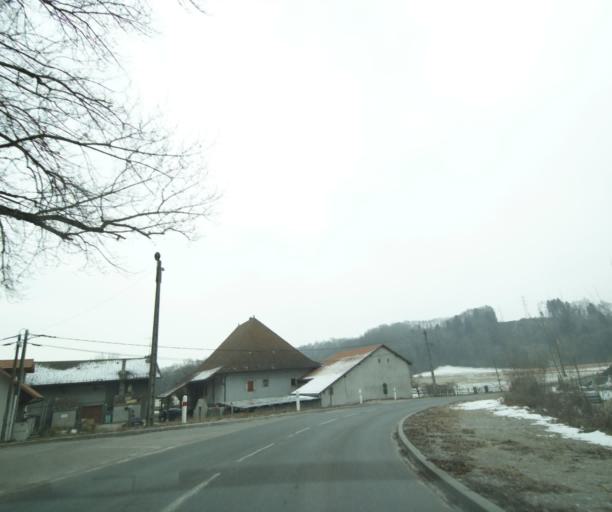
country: FR
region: Rhone-Alpes
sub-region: Departement de la Haute-Savoie
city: Arthaz-Pont-Notre-Dame
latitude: 46.1501
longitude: 6.2713
